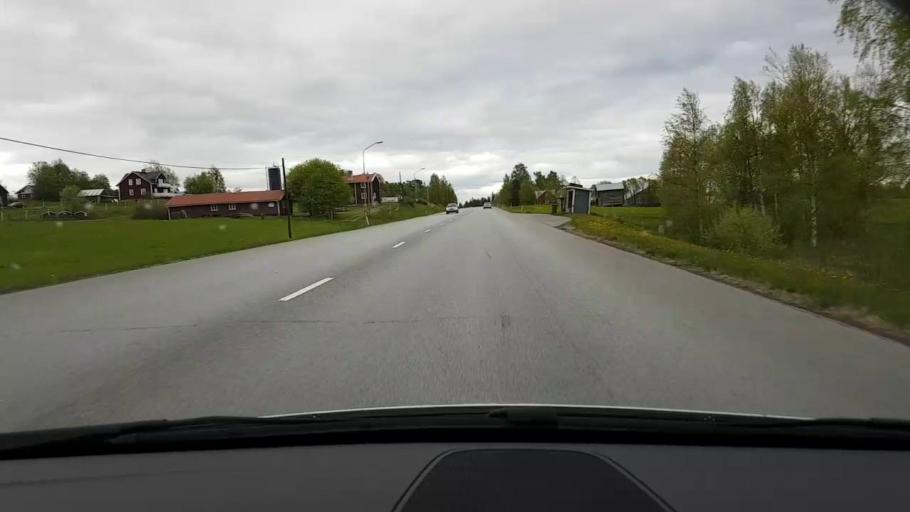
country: SE
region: Jaemtland
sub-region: Krokoms Kommun
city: Krokom
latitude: 63.3174
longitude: 14.0876
